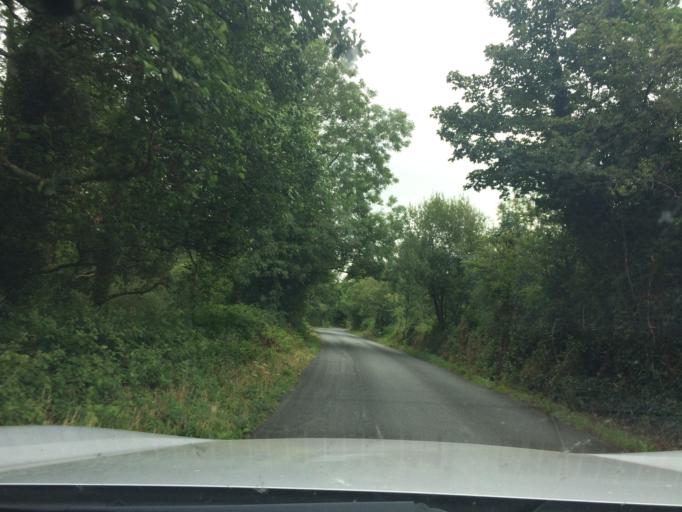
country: IE
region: Munster
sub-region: Waterford
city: Dungarvan
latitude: 52.1984
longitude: -7.7278
